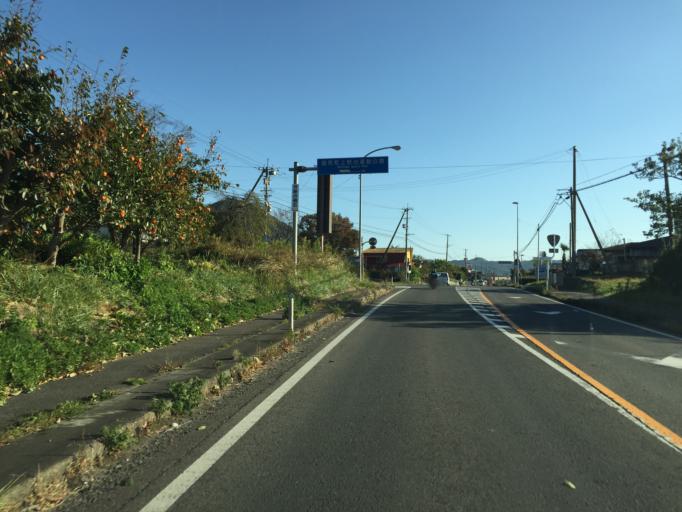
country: JP
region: Fukushima
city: Yanagawamachi-saiwaicho
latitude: 37.8827
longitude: 140.5559
